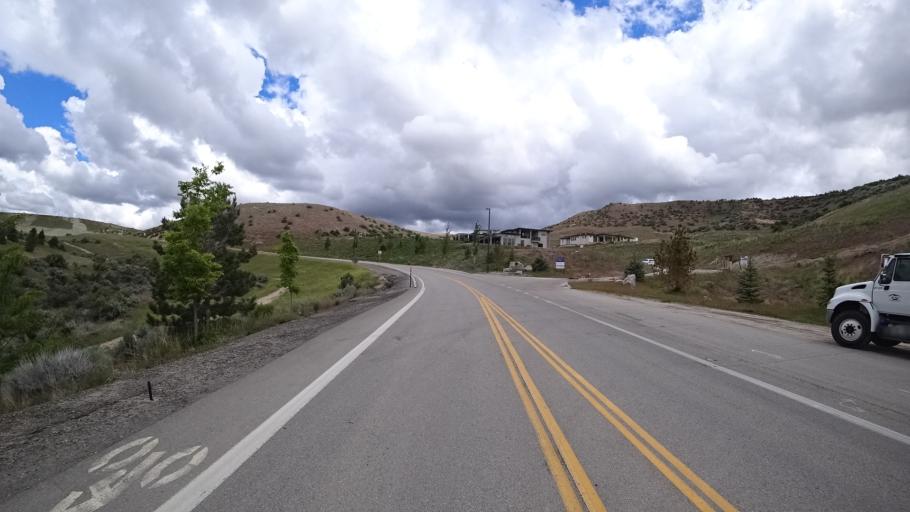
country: US
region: Idaho
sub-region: Ada County
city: Boise
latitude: 43.6610
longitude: -116.1899
